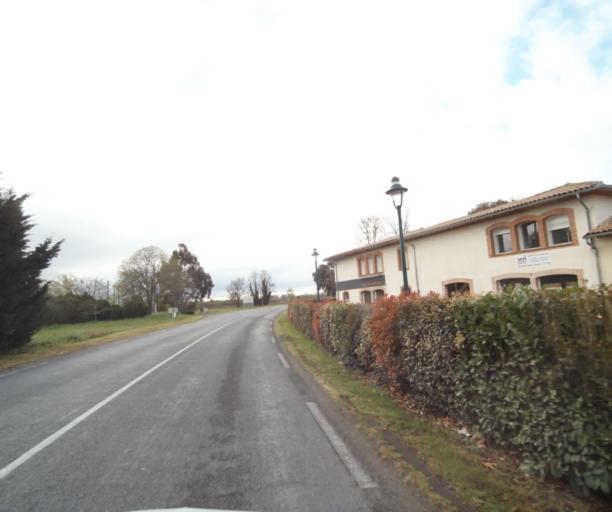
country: FR
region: Midi-Pyrenees
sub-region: Departement de l'Ariege
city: Saverdun
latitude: 43.2304
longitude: 1.6011
